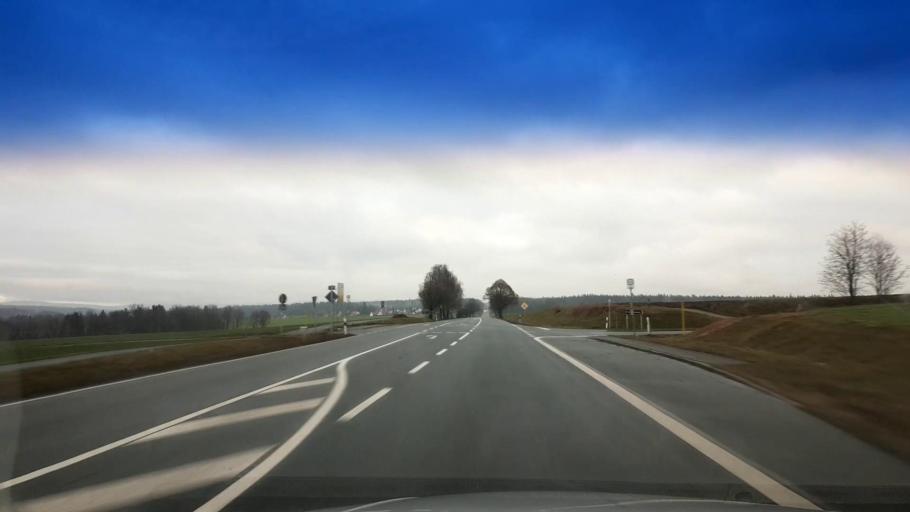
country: DE
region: Bavaria
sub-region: Upper Palatinate
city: Leonberg
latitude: 49.9369
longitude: 12.2650
